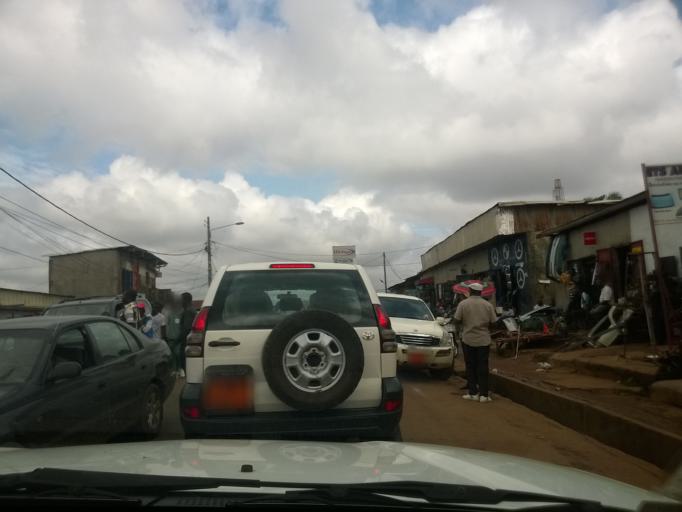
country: CM
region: Centre
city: Yaounde
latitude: 3.8644
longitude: 11.5291
